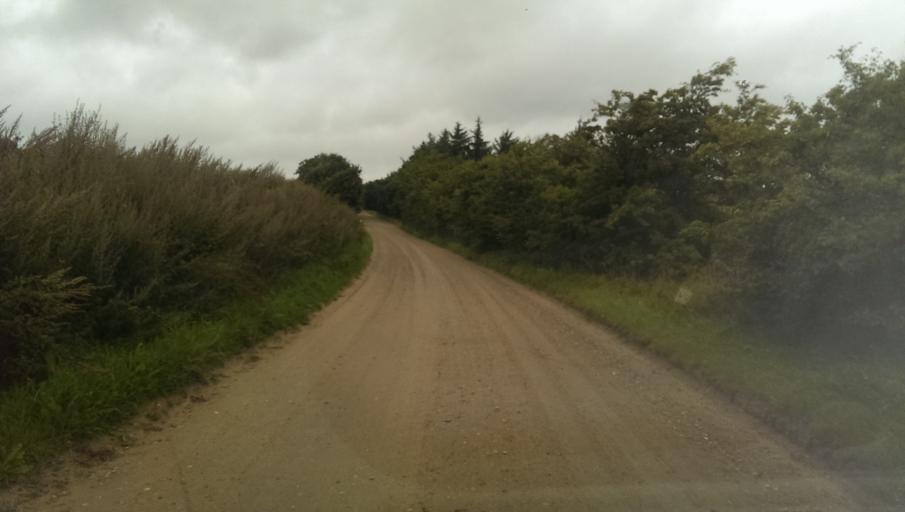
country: DK
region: South Denmark
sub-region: Esbjerg Kommune
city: Tjaereborg
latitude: 55.4805
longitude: 8.6010
